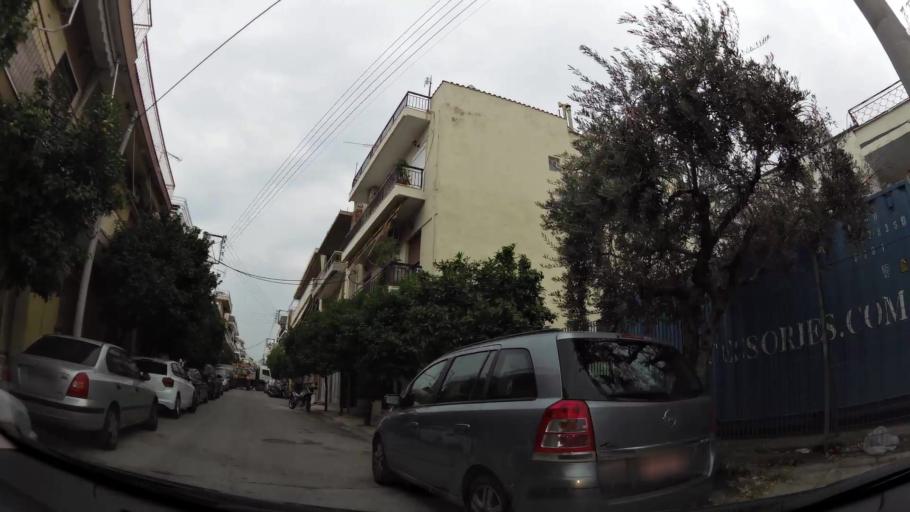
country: GR
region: Attica
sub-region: Nomarchia Athinas
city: Chaidari
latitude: 38.0068
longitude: 23.6734
